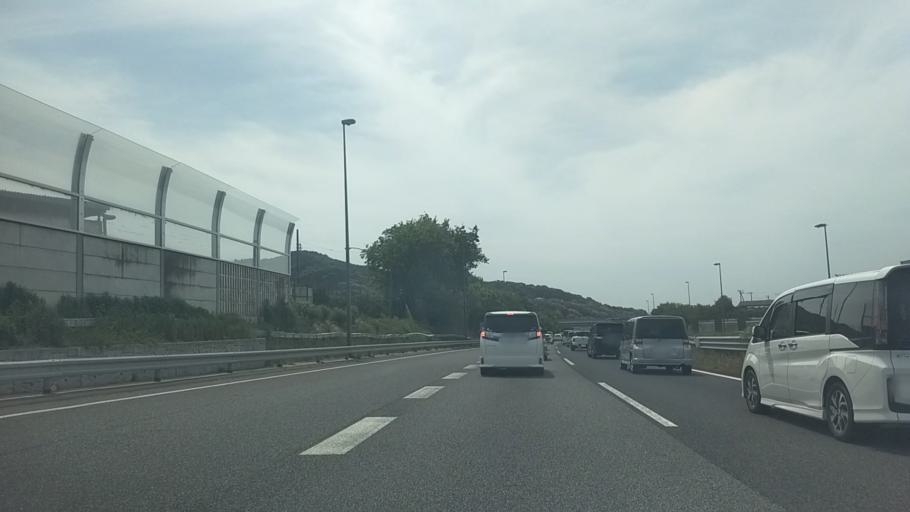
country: JP
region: Aichi
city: Shinshiro
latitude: 34.8216
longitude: 137.5495
